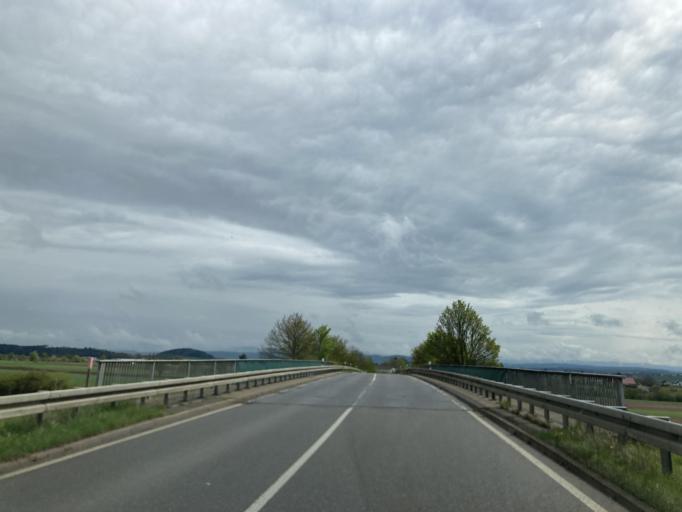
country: DE
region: Baden-Wuerttemberg
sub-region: Regierungsbezirk Stuttgart
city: Bondorf
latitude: 48.5162
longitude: 8.8695
